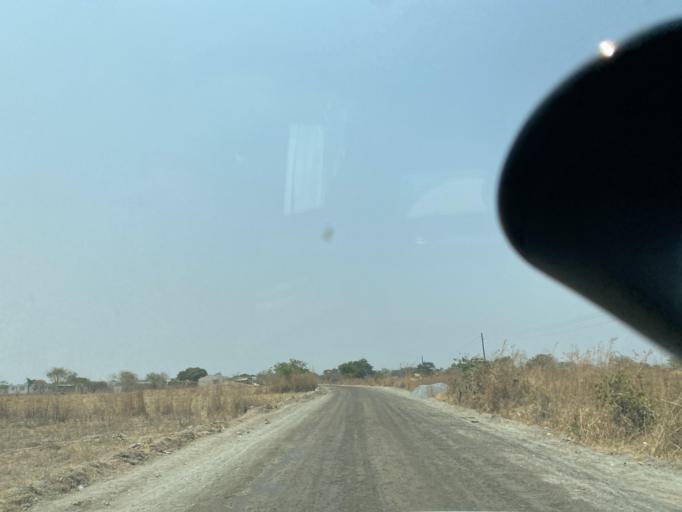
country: ZM
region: Lusaka
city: Lusaka
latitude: -15.5615
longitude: 28.4279
